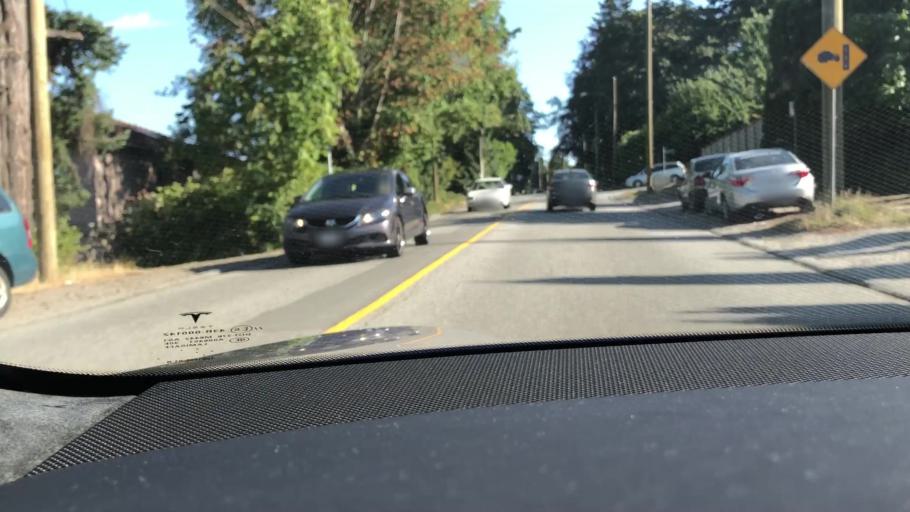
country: CA
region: British Columbia
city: Burnaby
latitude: 49.2540
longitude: -122.9820
